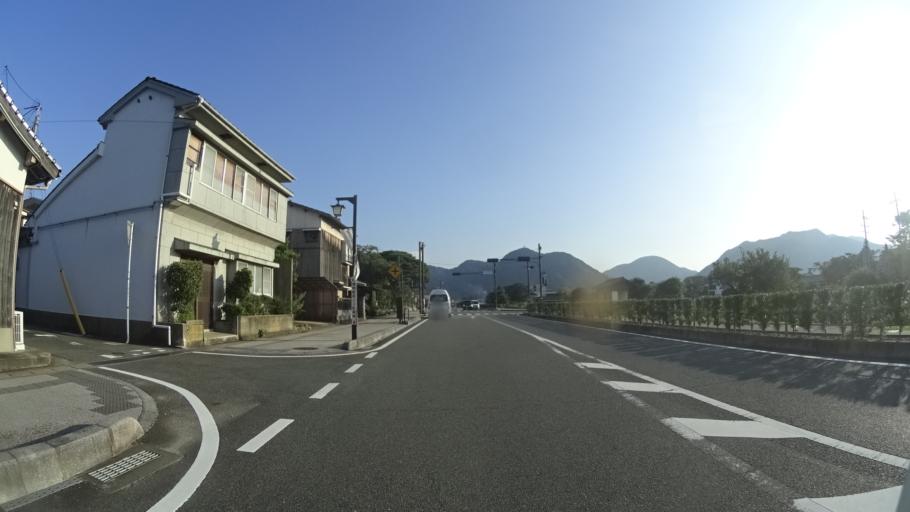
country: JP
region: Yamaguchi
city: Hagi
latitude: 34.4138
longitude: 131.3924
